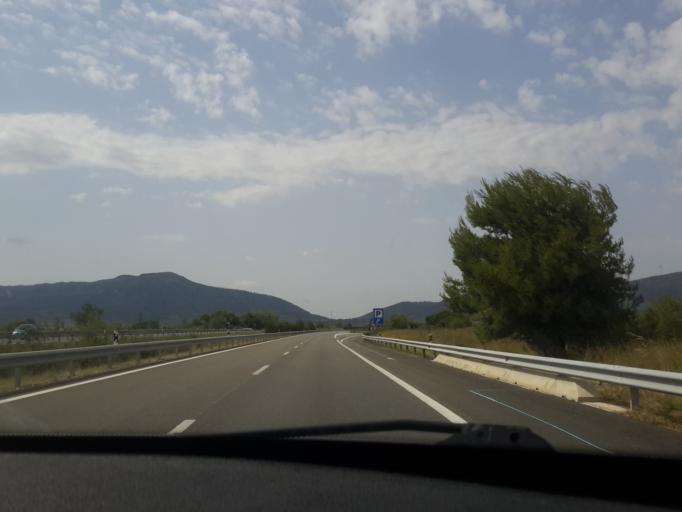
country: ES
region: Catalonia
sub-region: Provincia de Tarragona
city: El Pla de Santa Maria
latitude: 41.3498
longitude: 1.3168
